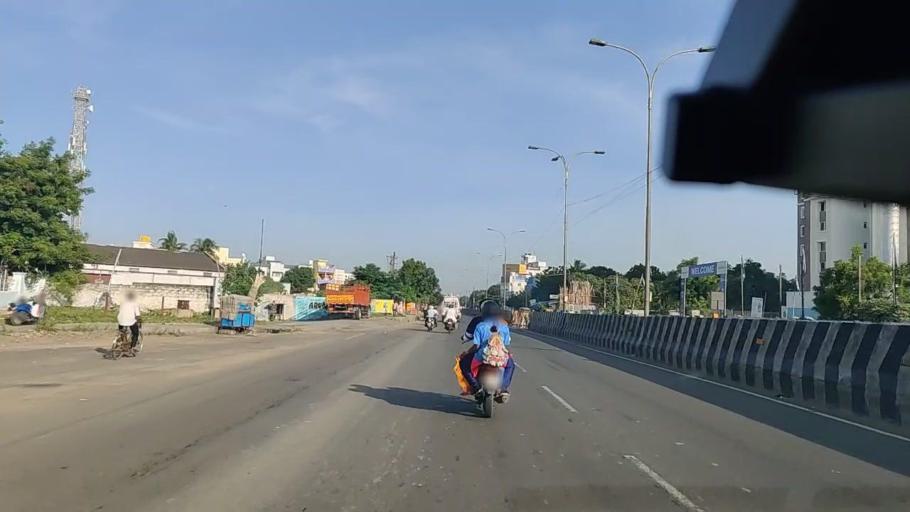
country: IN
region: Tamil Nadu
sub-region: Thiruvallur
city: Chinnasekkadu
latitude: 13.1353
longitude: 80.2327
